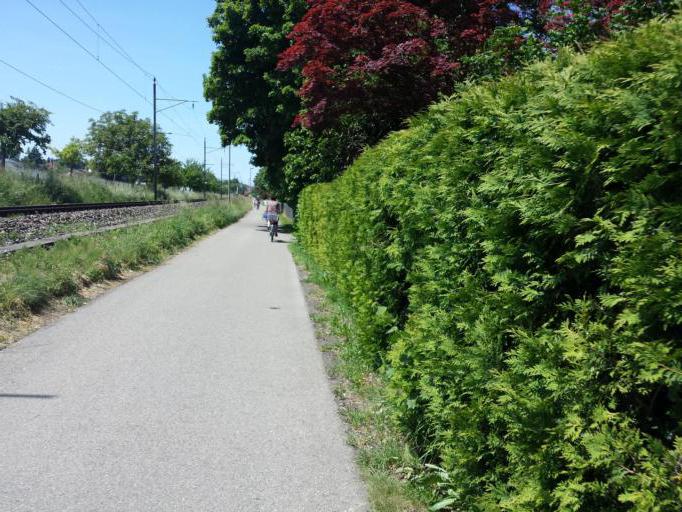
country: CH
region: Thurgau
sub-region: Arbon District
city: Uttwil
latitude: 47.5817
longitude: 9.3526
